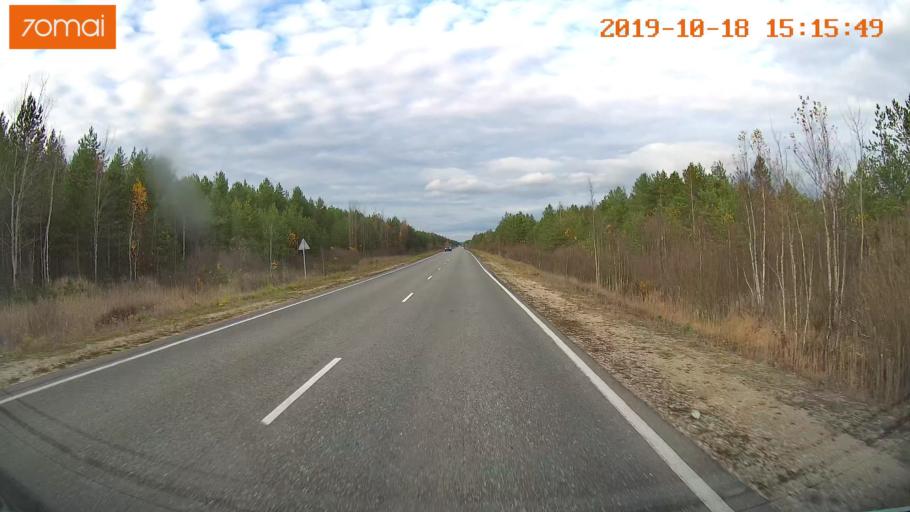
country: RU
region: Vladimir
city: Gus'-Khrustal'nyy
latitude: 55.6255
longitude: 40.7233
